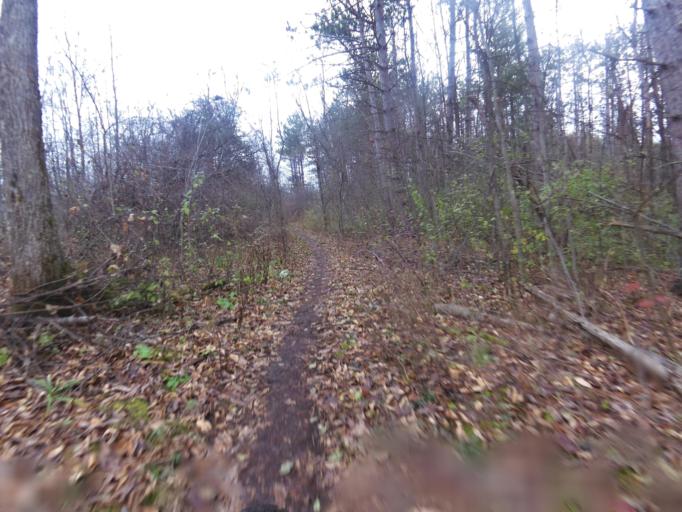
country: CA
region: Ontario
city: Bells Corners
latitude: 45.2868
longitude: -75.8340
